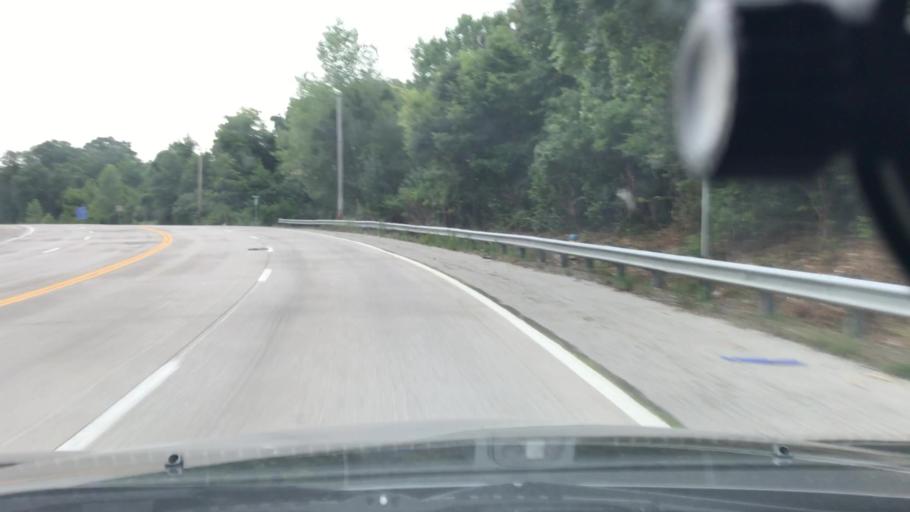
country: US
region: Missouri
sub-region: Saint Charles County
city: Saint Charles
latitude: 38.7430
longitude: -90.5238
